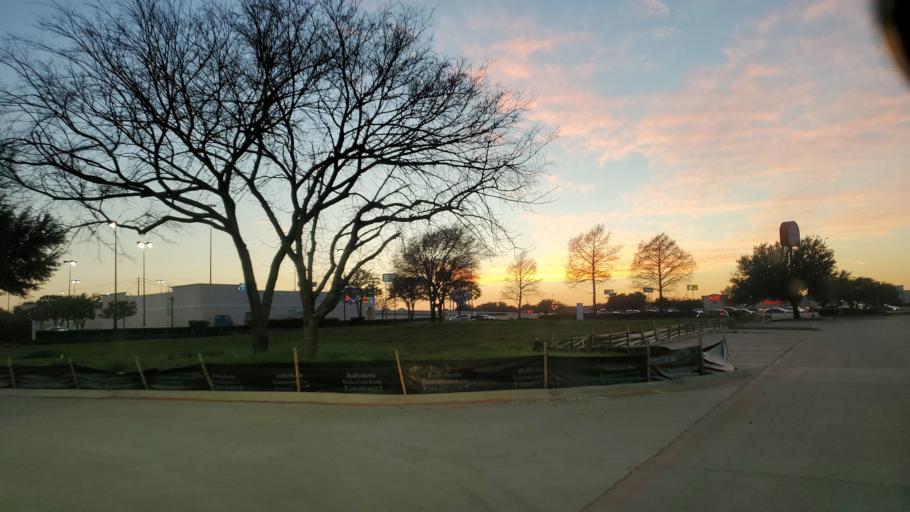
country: US
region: Texas
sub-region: Collin County
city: Plano
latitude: 33.0400
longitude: -96.7014
